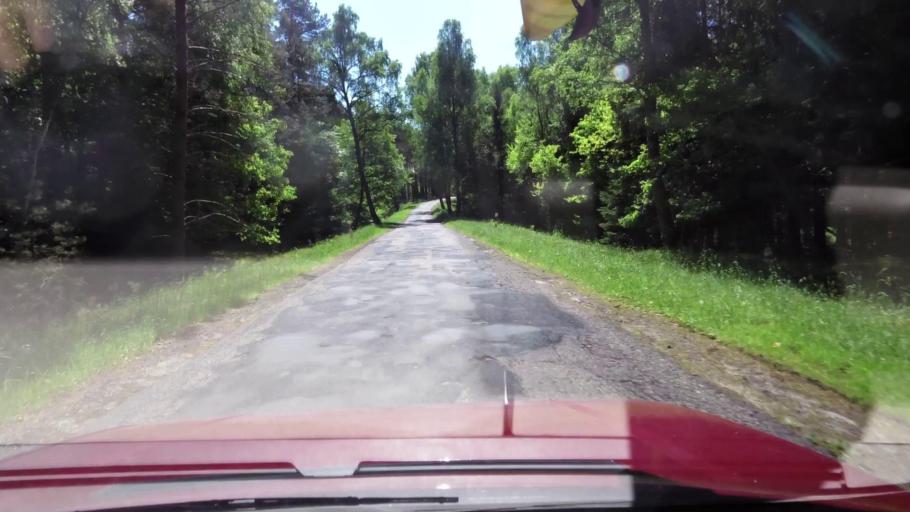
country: PL
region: West Pomeranian Voivodeship
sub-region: Powiat koszalinski
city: Bobolice
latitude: 54.0622
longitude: 16.5687
